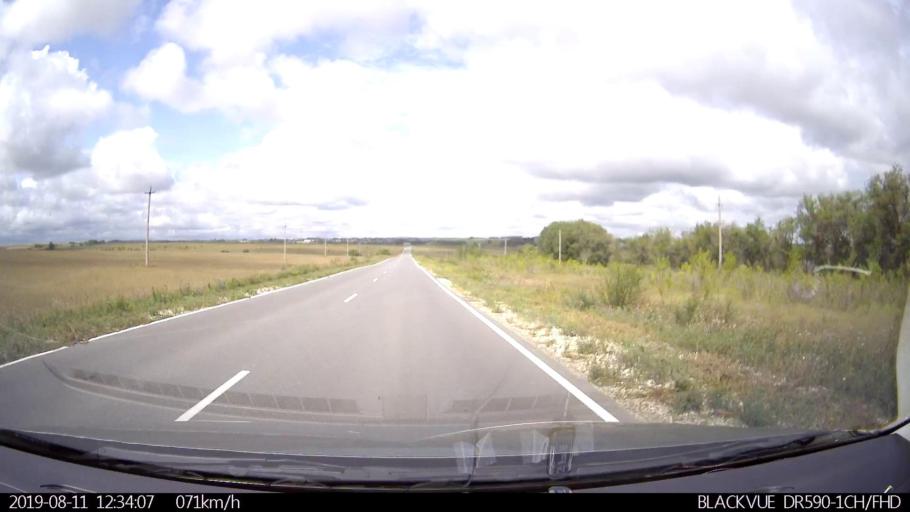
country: RU
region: Ulyanovsk
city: Ignatovka
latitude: 53.8145
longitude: 47.8470
